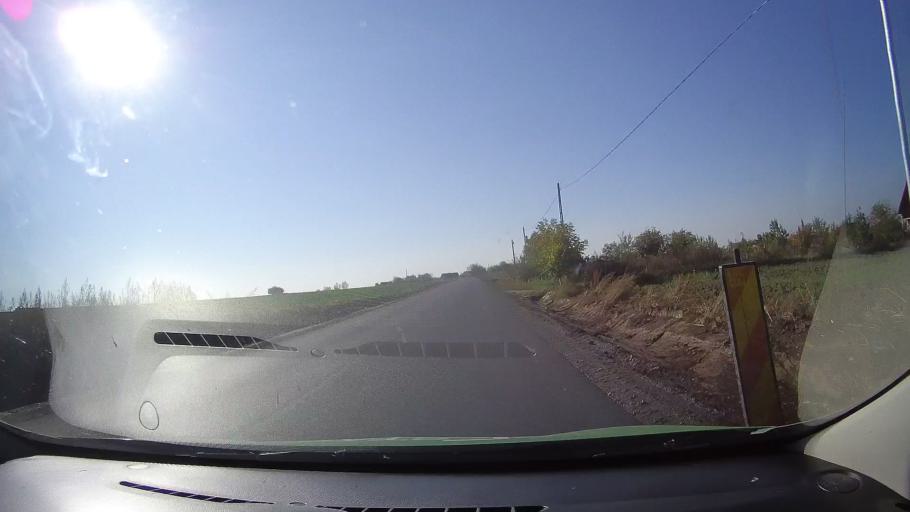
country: RO
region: Satu Mare
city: Carei
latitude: 47.6611
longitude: 22.4600
